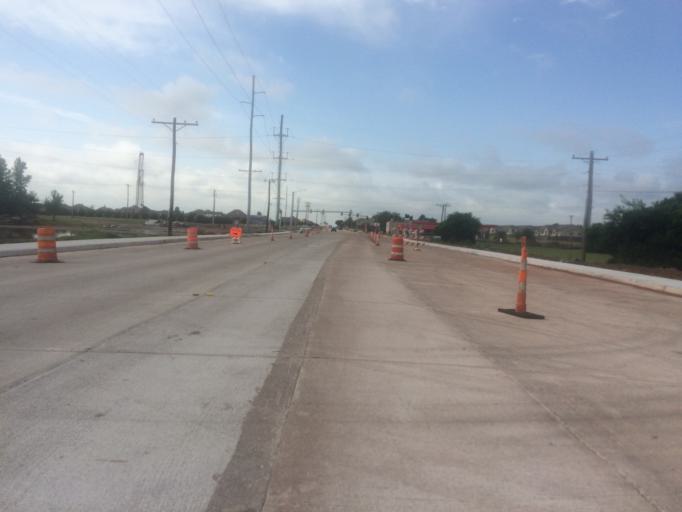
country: US
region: Oklahoma
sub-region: Cleveland County
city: Noble
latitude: 35.1769
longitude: -97.4237
